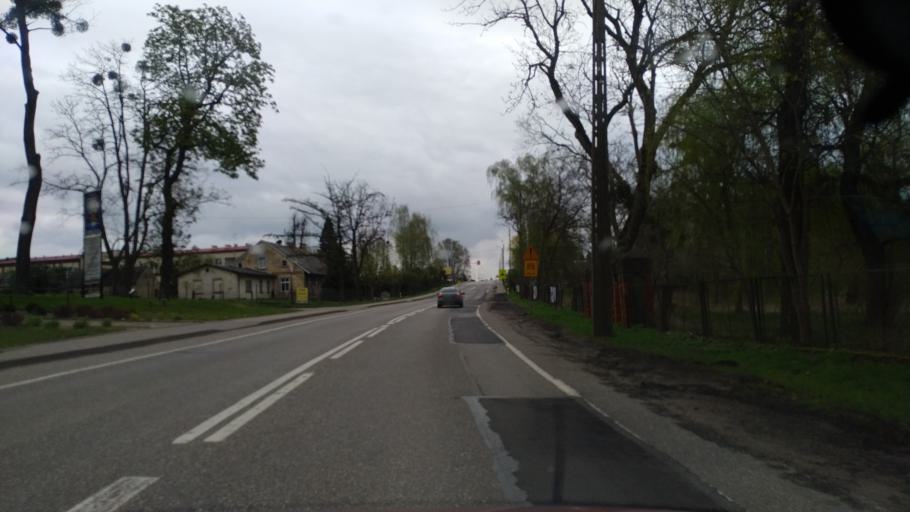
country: PL
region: Pomeranian Voivodeship
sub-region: Powiat tczewski
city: Subkowy
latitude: 54.0372
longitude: 18.6613
